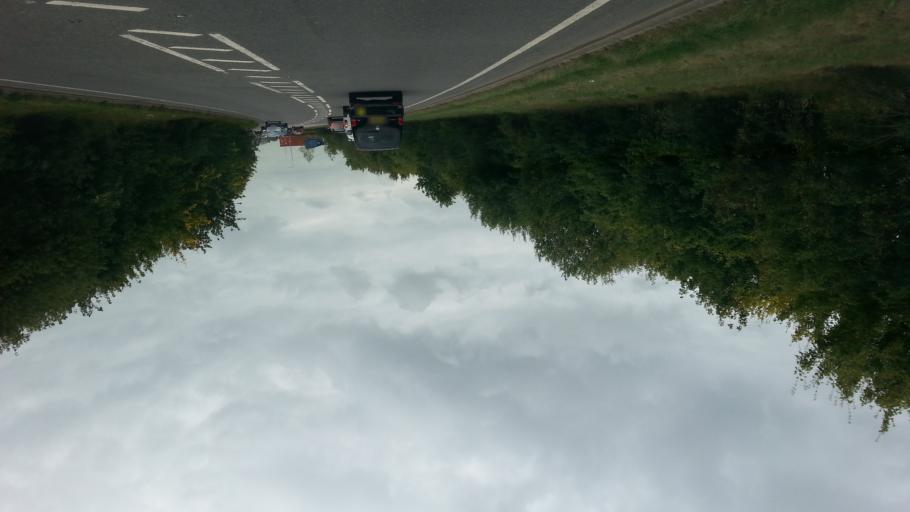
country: GB
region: England
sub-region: Essex
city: Chelmsford
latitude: 51.7669
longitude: 0.4876
